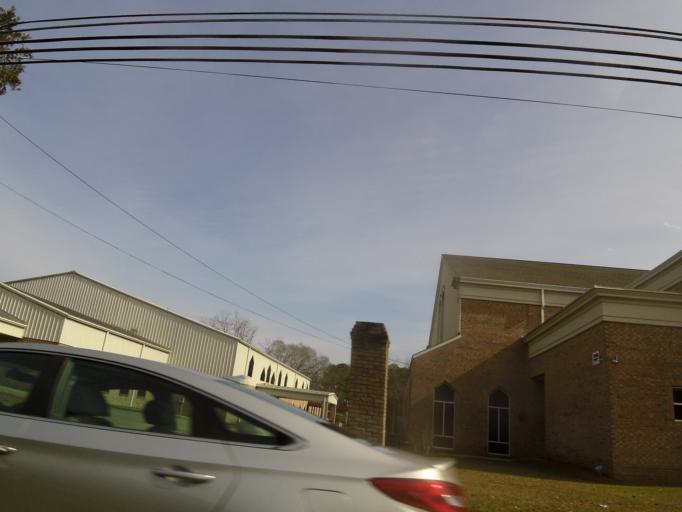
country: US
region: Alabama
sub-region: Houston County
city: Dothan
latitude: 31.2325
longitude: -85.3922
